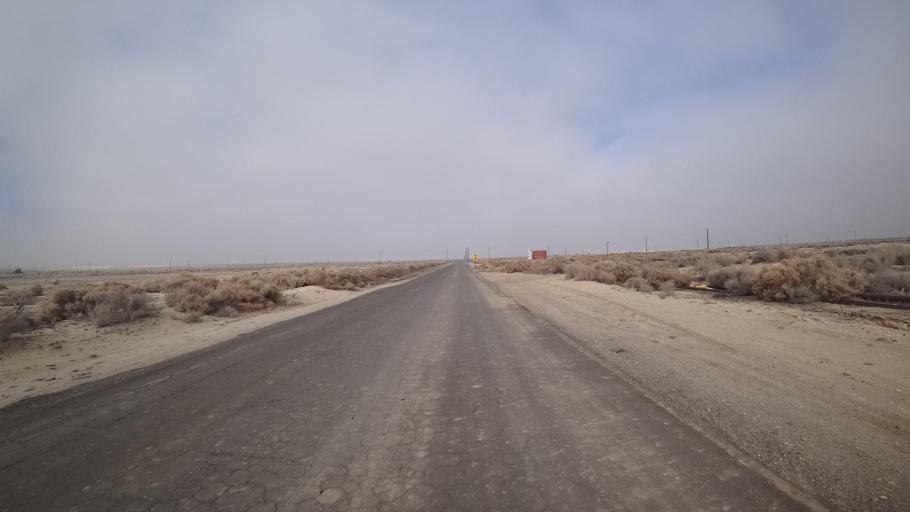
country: US
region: California
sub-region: Kern County
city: Maricopa
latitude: 35.0553
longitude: -119.3671
